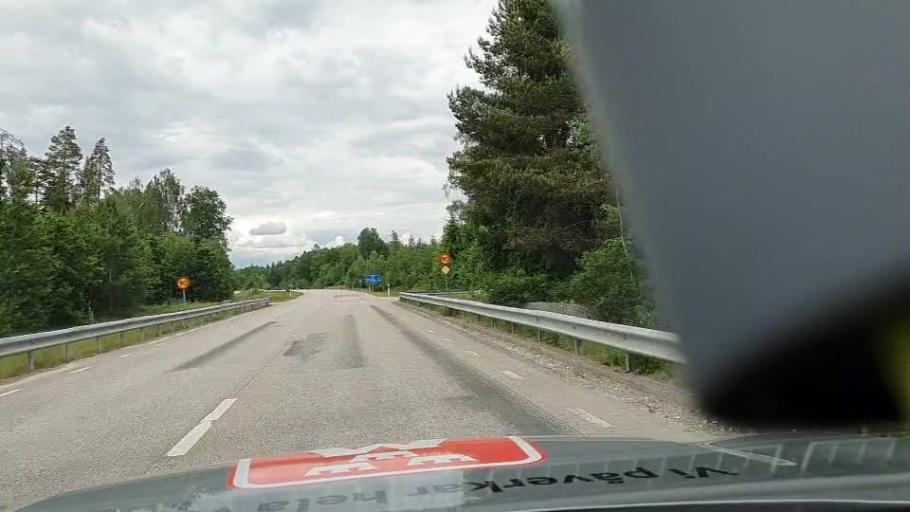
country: SE
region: Kalmar
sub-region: Emmaboda Kommun
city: Emmaboda
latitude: 56.4752
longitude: 15.5981
